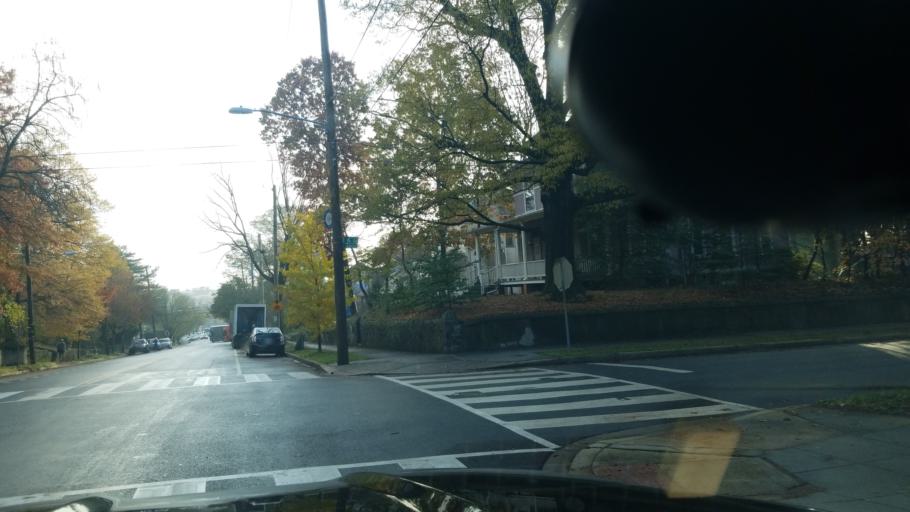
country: US
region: Maryland
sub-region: Montgomery County
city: Takoma Park
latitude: 38.9736
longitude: -77.0216
